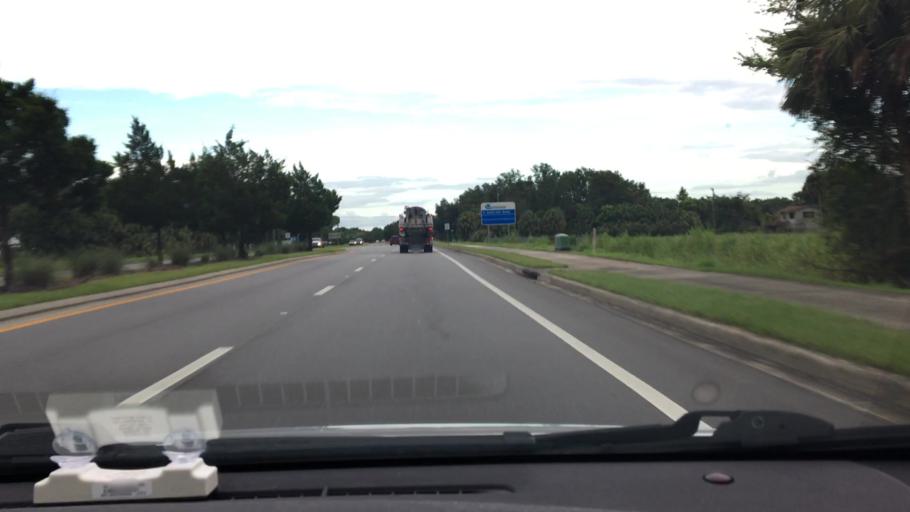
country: US
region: Florida
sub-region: Seminole County
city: Midway
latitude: 28.7604
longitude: -81.2246
